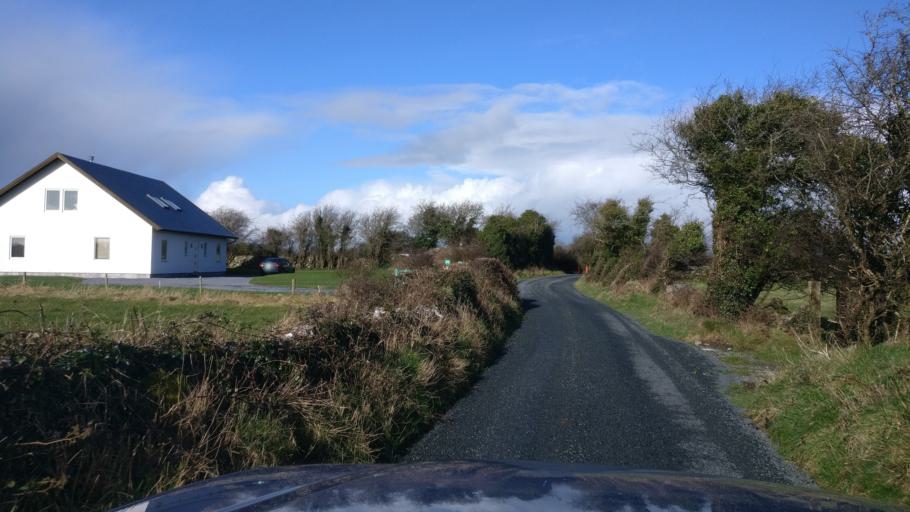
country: IE
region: Connaught
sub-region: County Galway
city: Athenry
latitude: 53.2384
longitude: -8.7742
